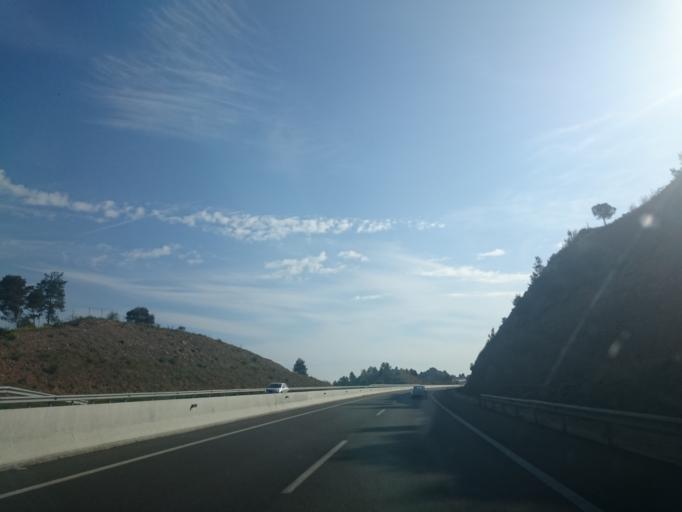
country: ES
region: Catalonia
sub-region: Provincia de Barcelona
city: Santa Maria d'Olo
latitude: 41.8794
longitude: 2.0245
